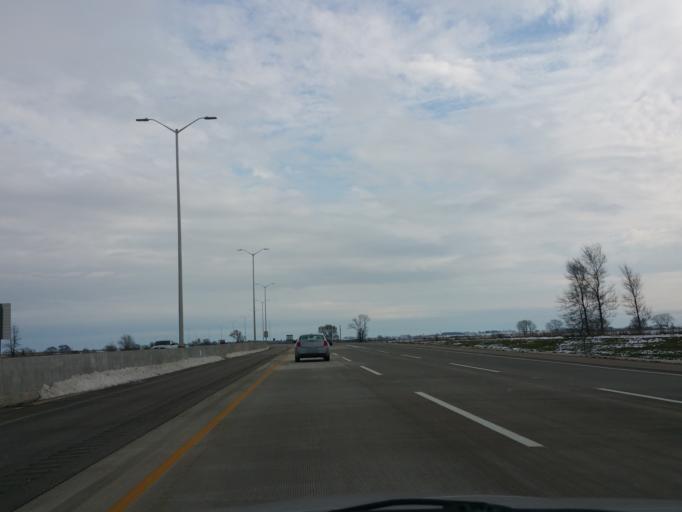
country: US
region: Illinois
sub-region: Winnebago County
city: Cherry Valley
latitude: 42.2375
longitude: -88.9147
